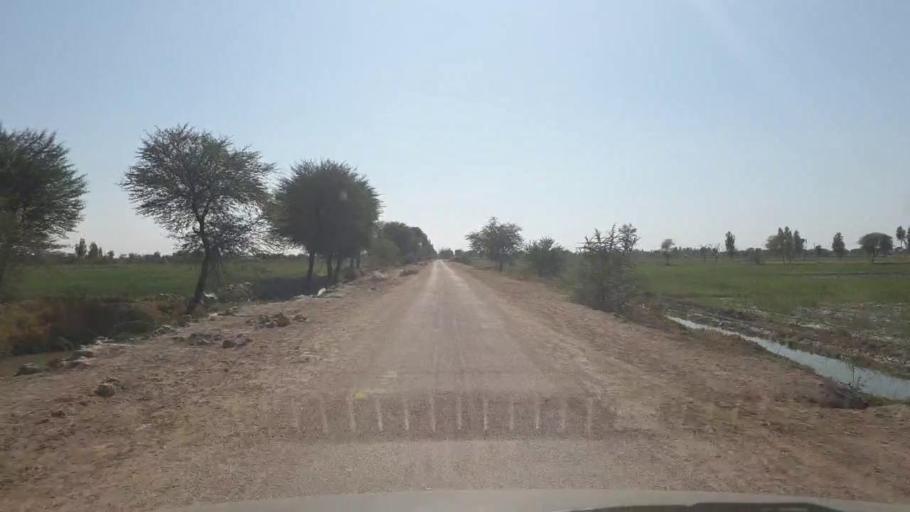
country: PK
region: Sindh
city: Dhoro Naro
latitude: 25.4018
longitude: 69.5968
